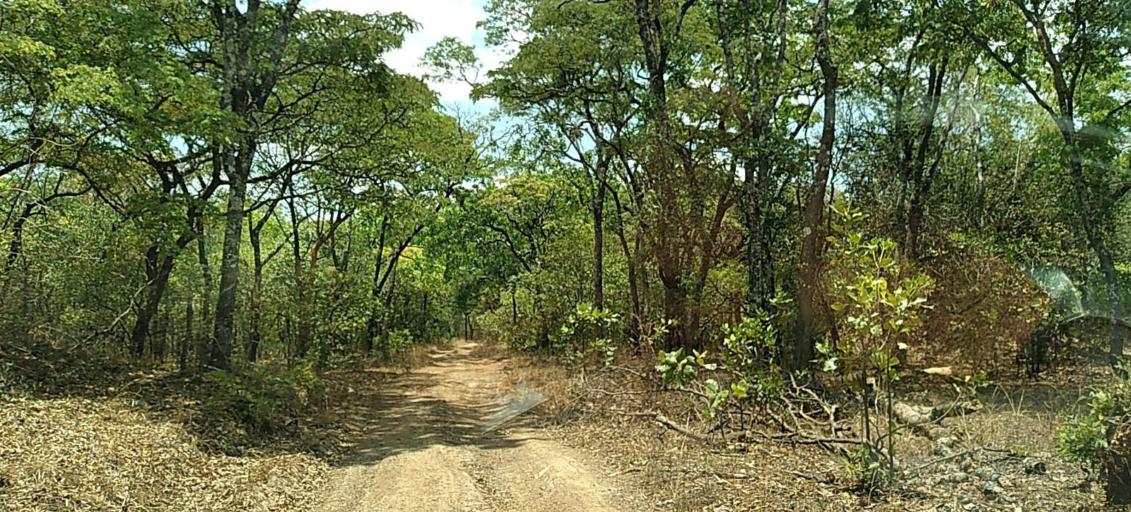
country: ZM
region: Copperbelt
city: Chililabombwe
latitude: -12.4634
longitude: 27.6991
